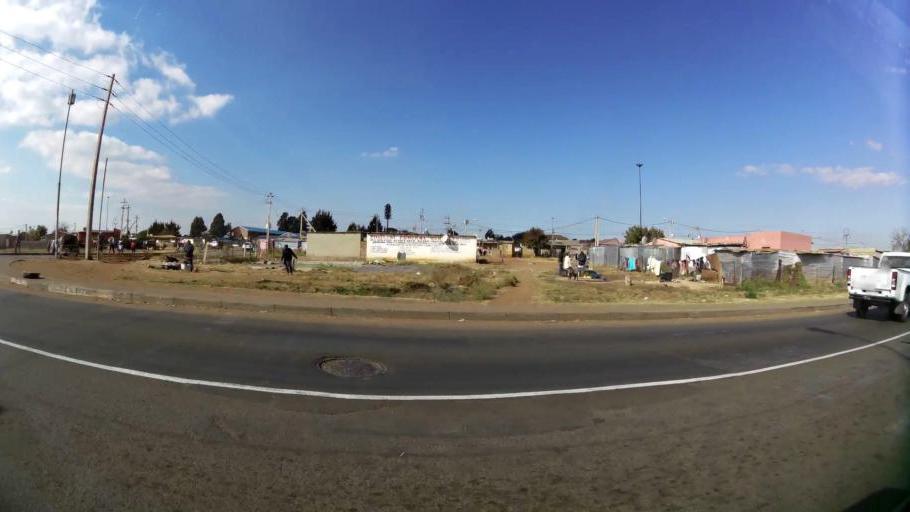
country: ZA
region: Gauteng
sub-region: City of Johannesburg Metropolitan Municipality
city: Soweto
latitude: -26.2713
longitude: 27.8905
